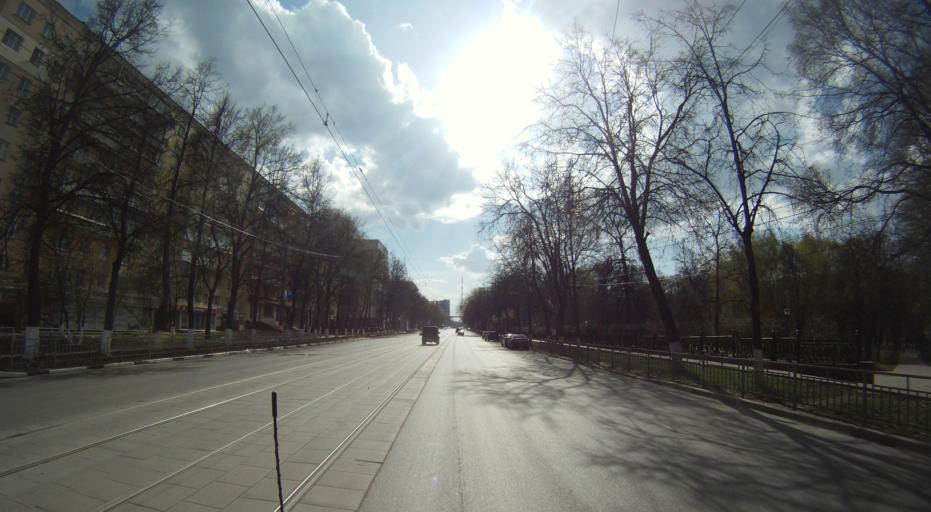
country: RU
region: Nizjnij Novgorod
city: Nizhniy Novgorod
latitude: 56.3148
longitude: 44.0119
